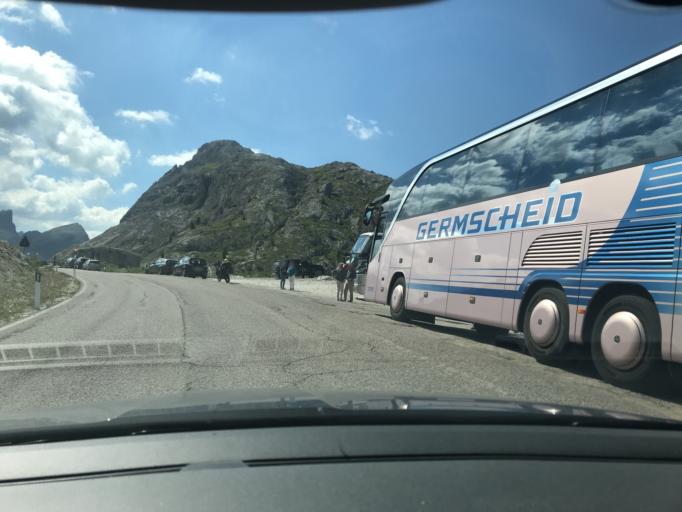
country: IT
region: Veneto
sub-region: Provincia di Belluno
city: Livinallongo del Col di Lana
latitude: 46.5292
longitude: 11.9899
